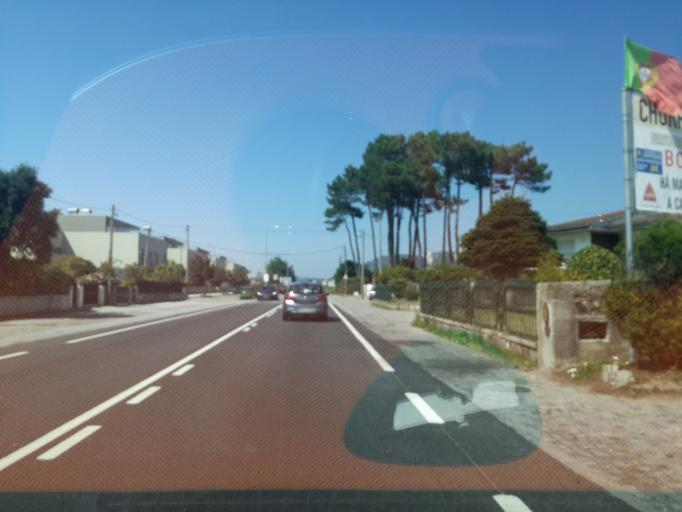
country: PT
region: Braga
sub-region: Esposende
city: Esposende
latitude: 41.5465
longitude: -8.7824
